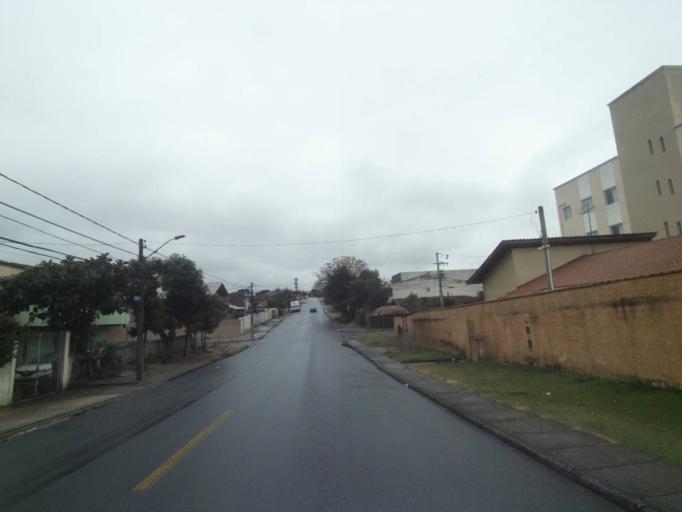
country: BR
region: Parana
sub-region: Curitiba
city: Curitiba
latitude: -25.5064
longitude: -49.3010
